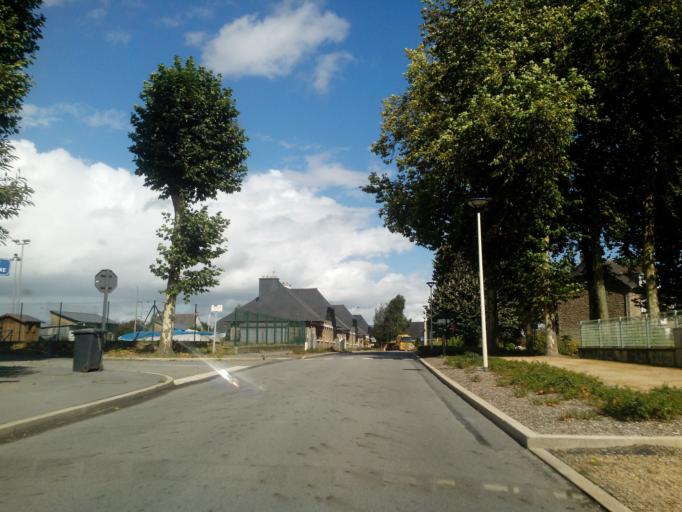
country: FR
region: Brittany
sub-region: Departement des Cotes-d'Armor
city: Merdrignac
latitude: 48.1948
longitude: -2.4195
